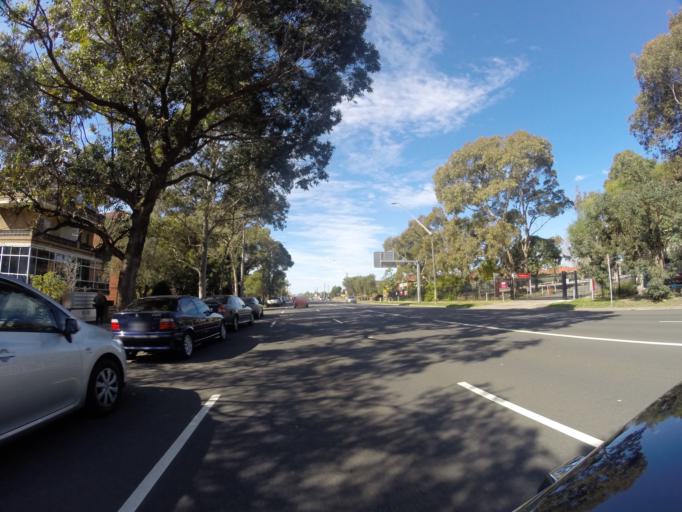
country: AU
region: New South Wales
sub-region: Rockdale
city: Monterey
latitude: -33.9645
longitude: 151.1388
